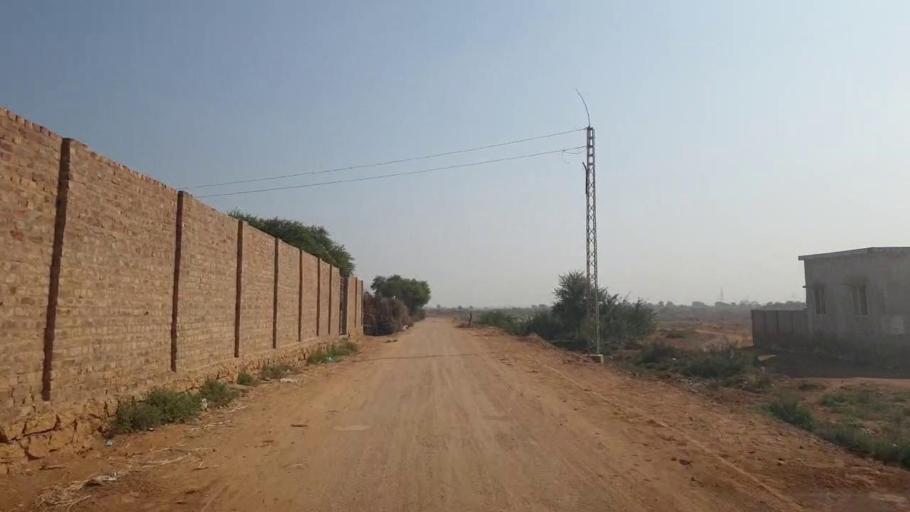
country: PK
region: Sindh
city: Jamshoro
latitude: 25.4619
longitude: 68.2905
